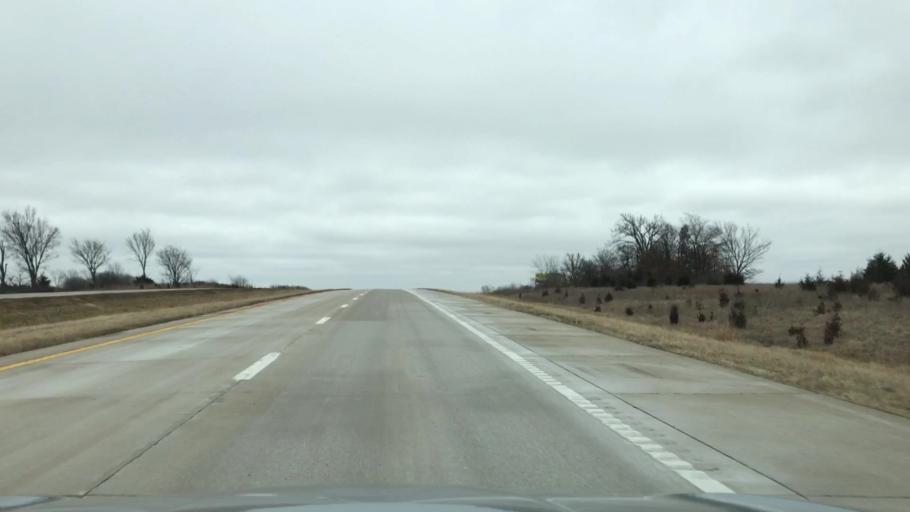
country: US
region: Missouri
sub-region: Livingston County
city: Chillicothe
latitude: 39.7357
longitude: -93.7465
